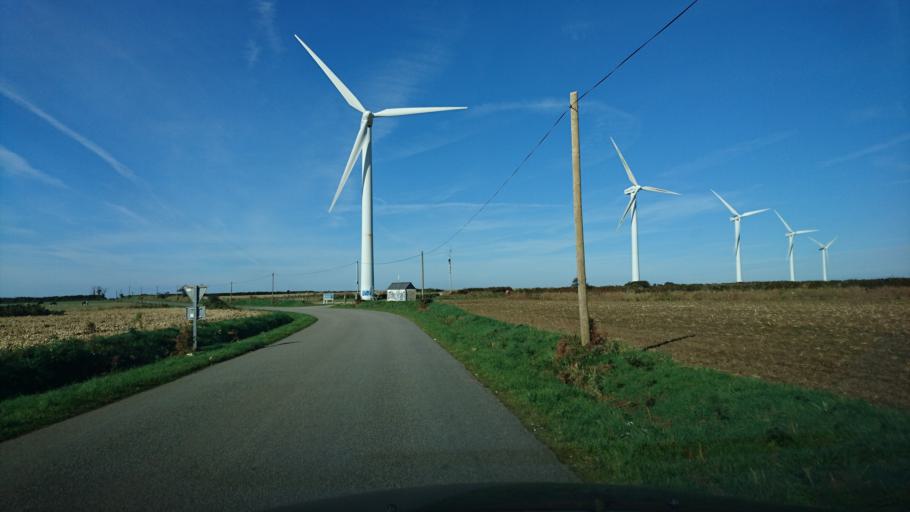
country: FR
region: Brittany
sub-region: Departement du Finistere
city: Plouarzel
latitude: 48.4275
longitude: -4.7463
